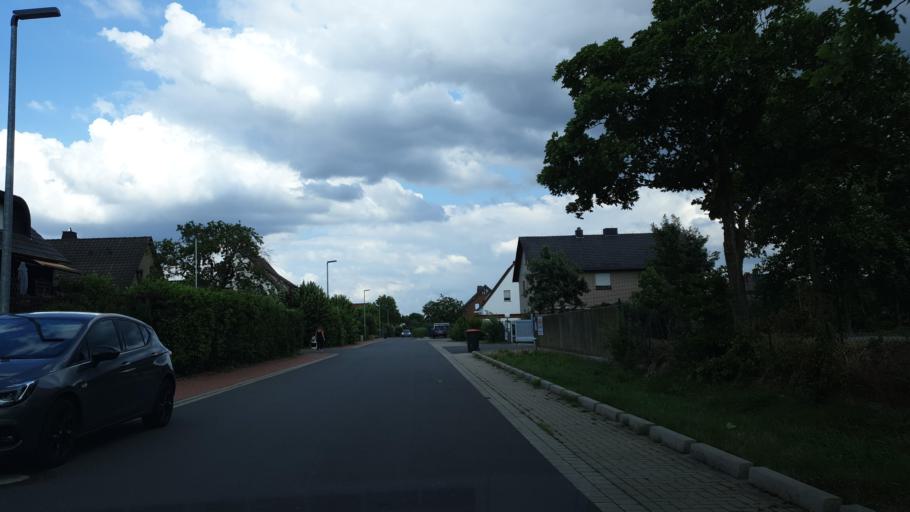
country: DE
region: North Rhine-Westphalia
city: Loehne
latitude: 52.2130
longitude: 8.7282
